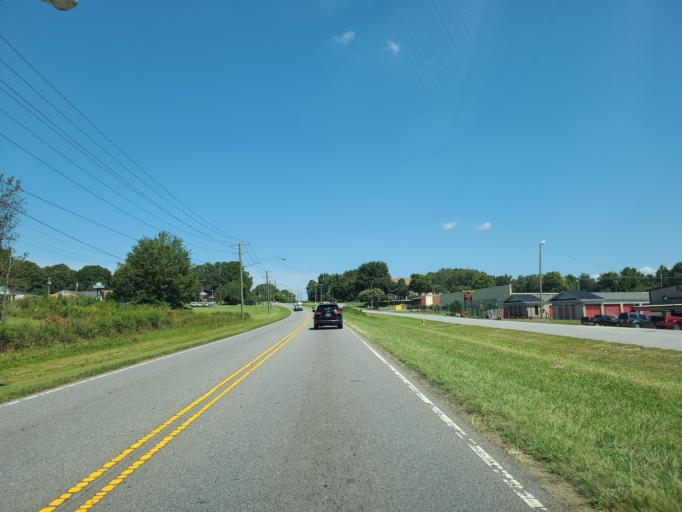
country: US
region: North Carolina
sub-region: Lincoln County
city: Lincolnton
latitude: 35.4692
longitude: -81.2396
